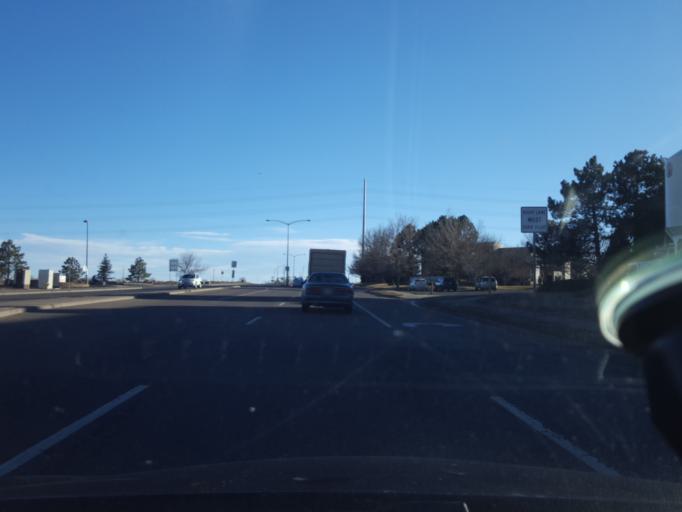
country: US
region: Colorado
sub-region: Adams County
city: Aurora
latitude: 39.7571
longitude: -104.7723
